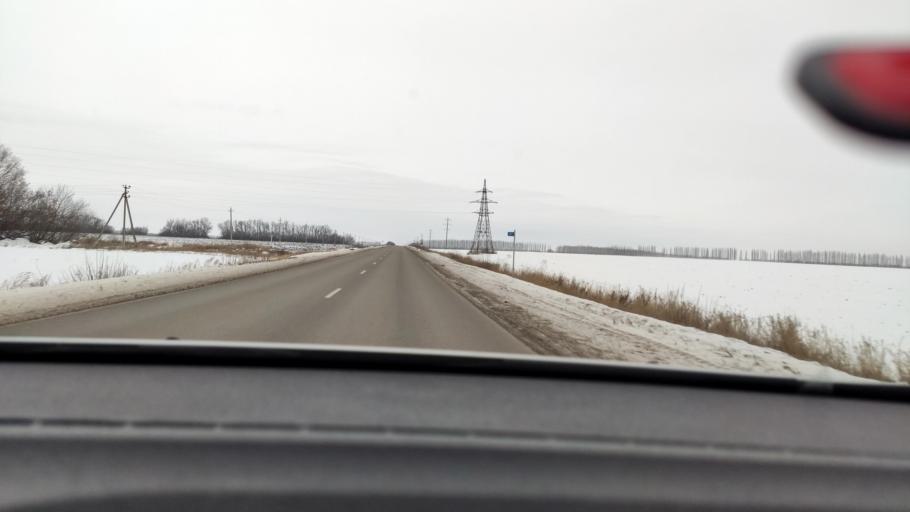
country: RU
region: Voronezj
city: Latnaya
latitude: 51.7400
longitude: 38.9428
